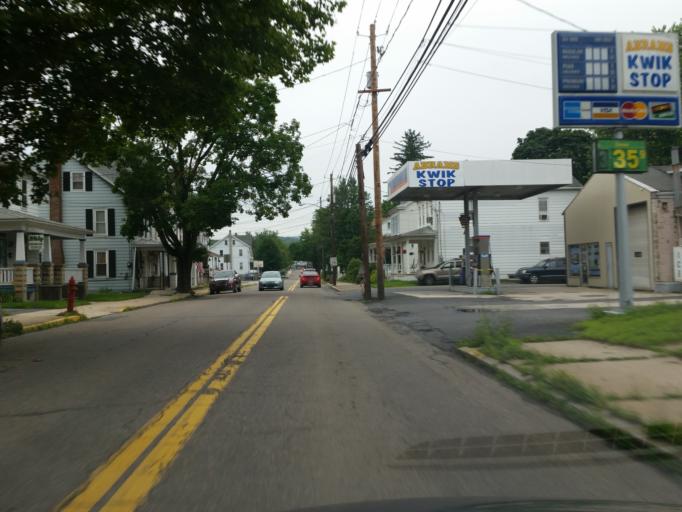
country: US
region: Pennsylvania
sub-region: Schuylkill County
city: Pine Grove
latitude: 40.5559
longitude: -76.3907
